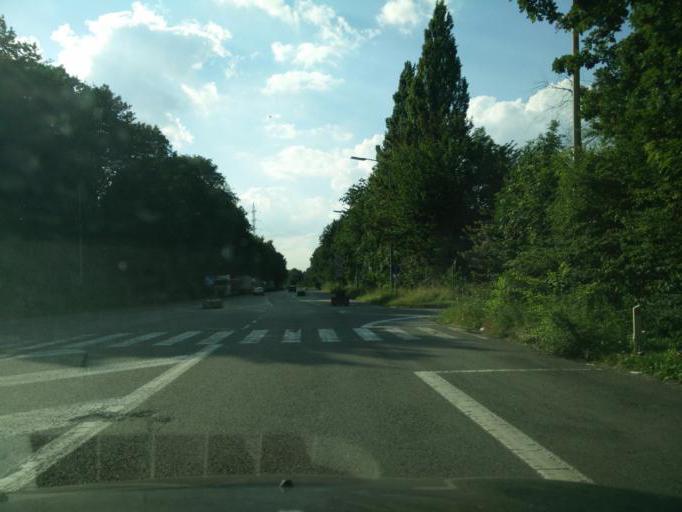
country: BE
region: Flanders
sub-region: Provincie Vlaams-Brabant
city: Halle
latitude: 50.7284
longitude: 4.2567
